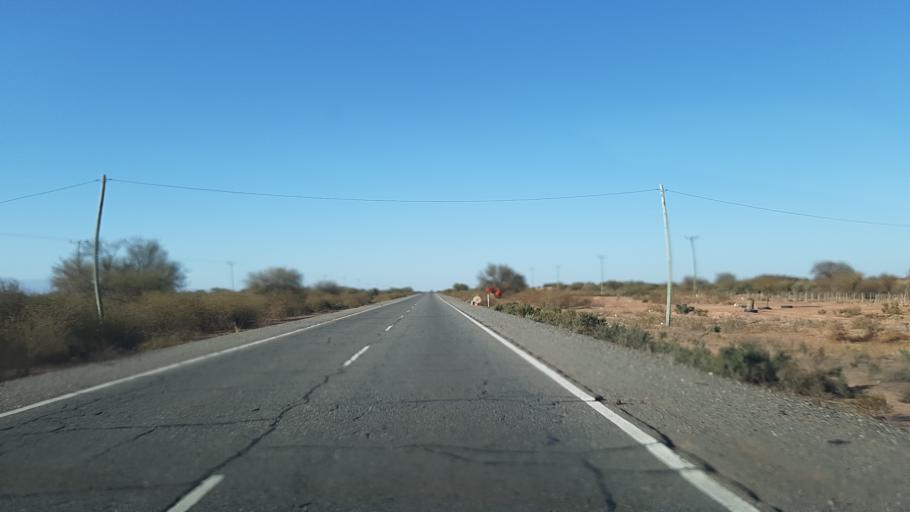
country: AR
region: San Juan
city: Caucete
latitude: -31.6055
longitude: -67.7114
